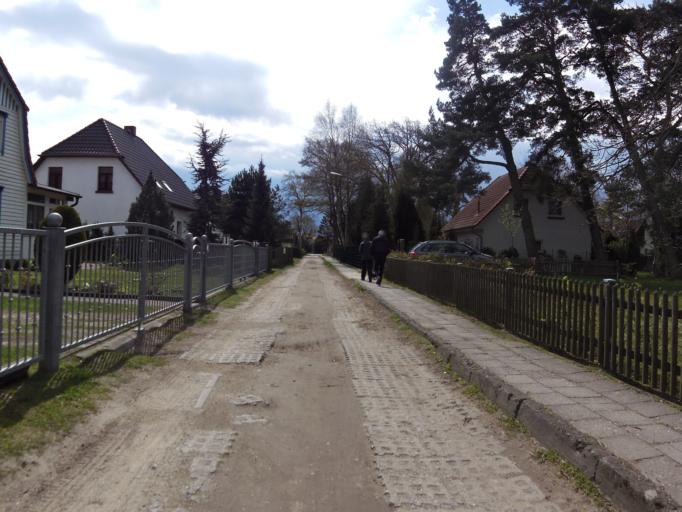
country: DE
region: Mecklenburg-Vorpommern
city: Ostseebad Prerow
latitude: 54.4487
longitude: 12.5646
